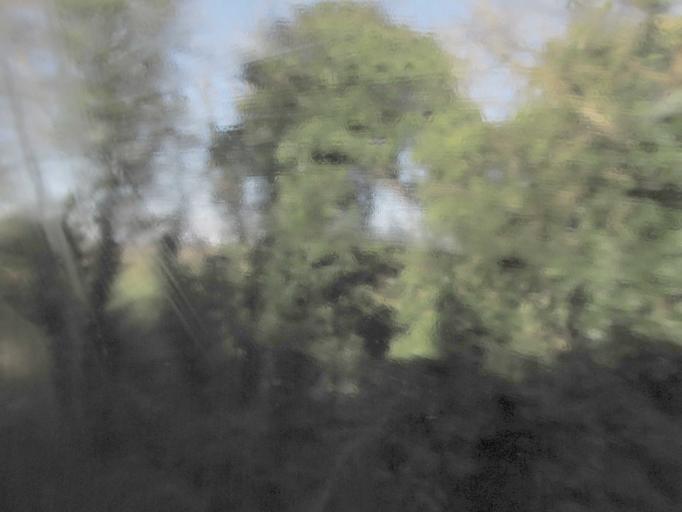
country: GB
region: England
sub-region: Hampshire
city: Overton
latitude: 51.1764
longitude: -1.2936
